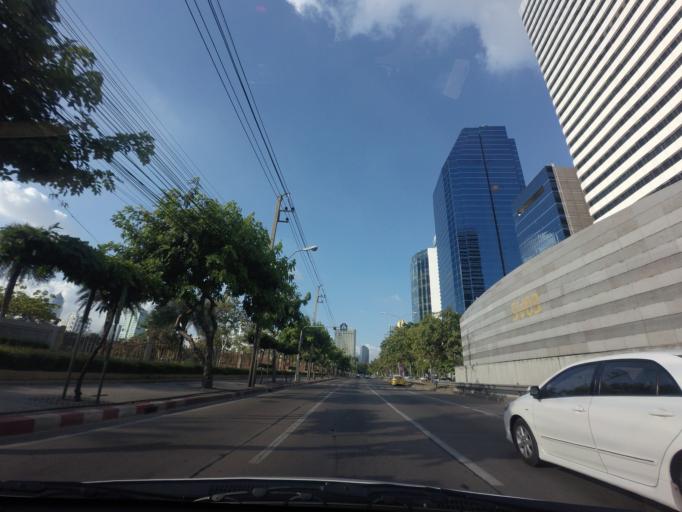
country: TH
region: Bangkok
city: Khlong Toei
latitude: 13.7300
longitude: 100.5595
